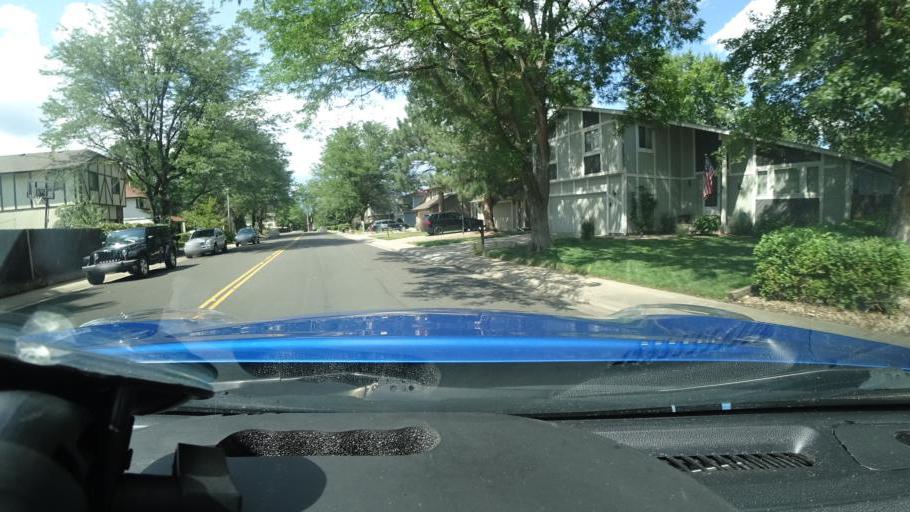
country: US
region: Colorado
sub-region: Adams County
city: Aurora
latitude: 39.6771
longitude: -104.8501
